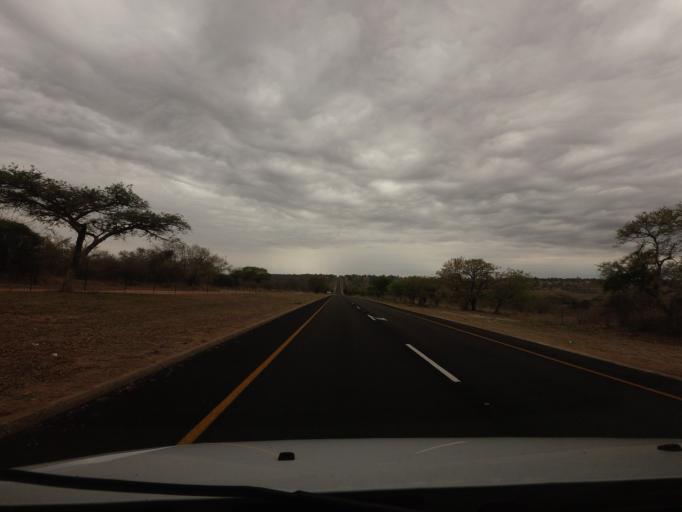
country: ZA
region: Limpopo
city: Thulamahashi
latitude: -24.5671
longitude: 31.0949
